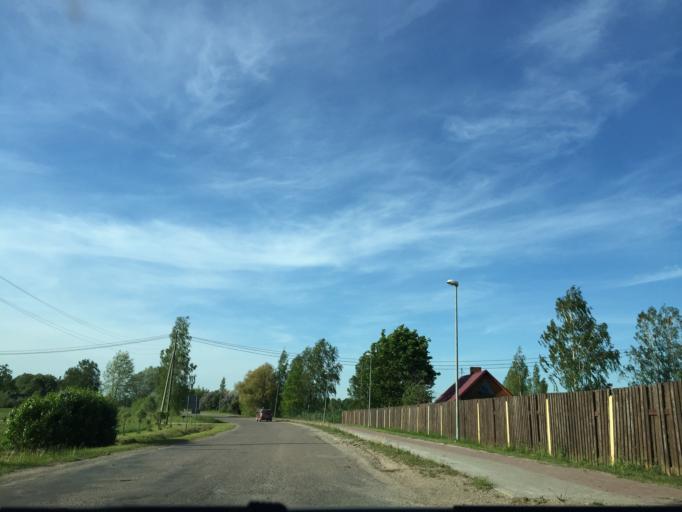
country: LV
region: Jelgava
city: Jelgava
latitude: 56.5929
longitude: 23.6792
